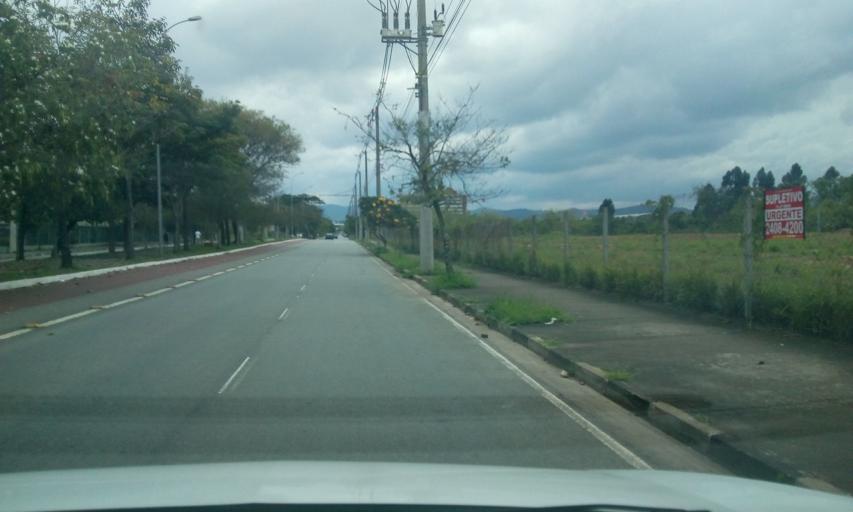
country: BR
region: Sao Paulo
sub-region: Guarulhos
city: Guarulhos
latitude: -23.4556
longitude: -46.4935
